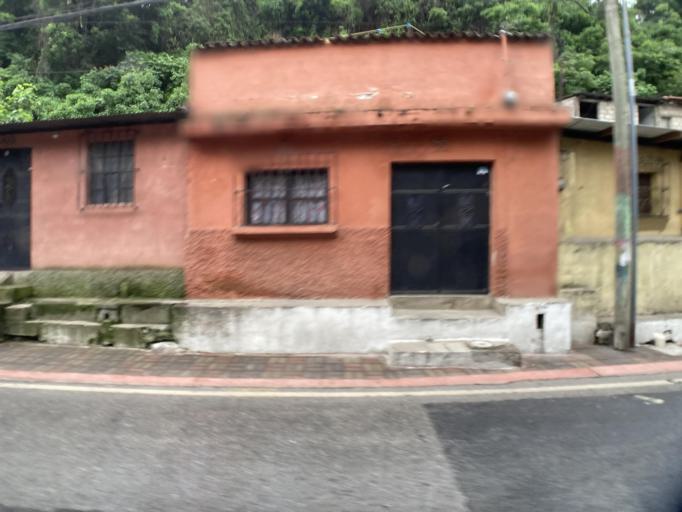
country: GT
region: Sacatepequez
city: Pastores
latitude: 14.6018
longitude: -90.7610
